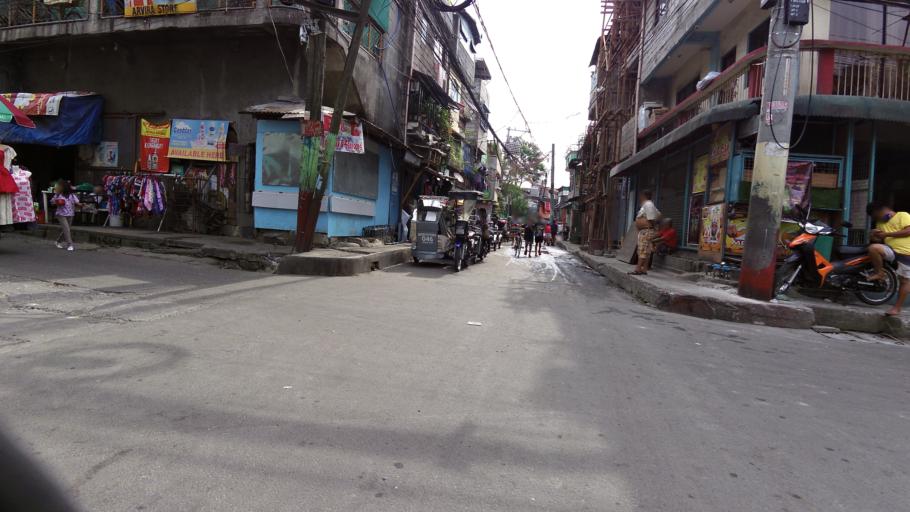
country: PH
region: Calabarzon
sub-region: Province of Rizal
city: Pateros
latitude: 14.5602
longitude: 121.0877
